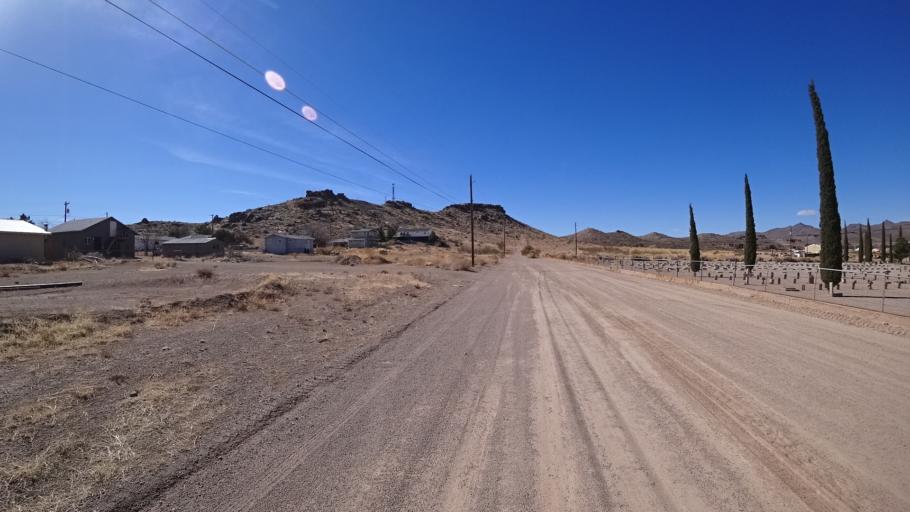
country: US
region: Arizona
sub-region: Mohave County
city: Kingman
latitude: 35.1994
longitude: -114.0347
